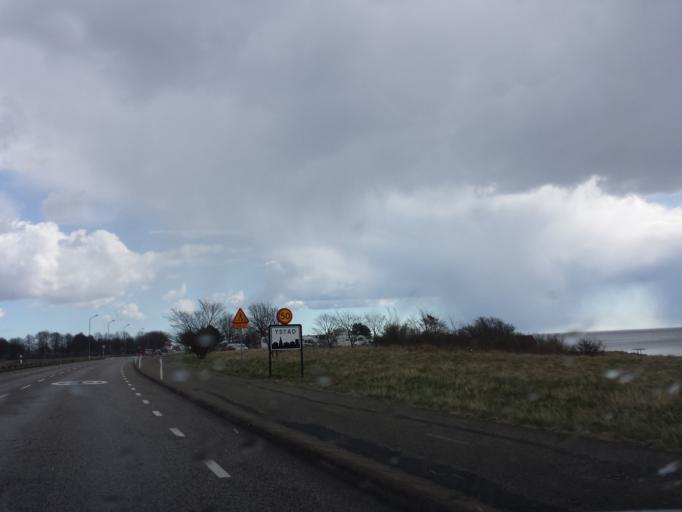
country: SE
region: Skane
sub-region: Ystads Kommun
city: Ystad
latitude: 55.4256
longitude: 13.7838
